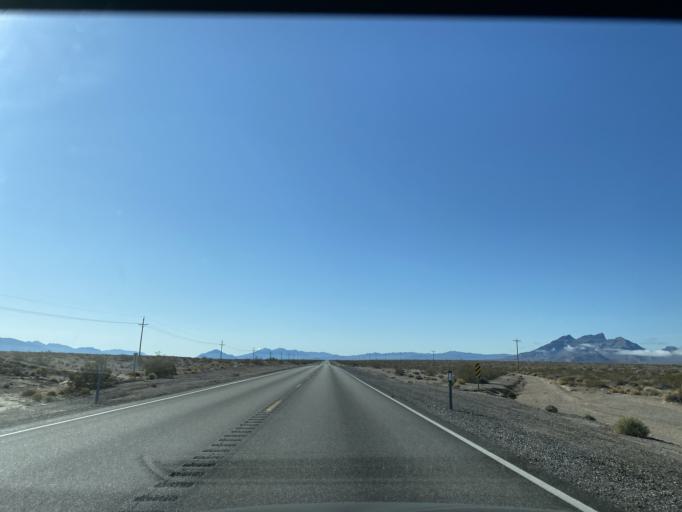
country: US
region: Nevada
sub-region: Nye County
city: Pahrump
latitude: 36.4759
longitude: -116.4216
